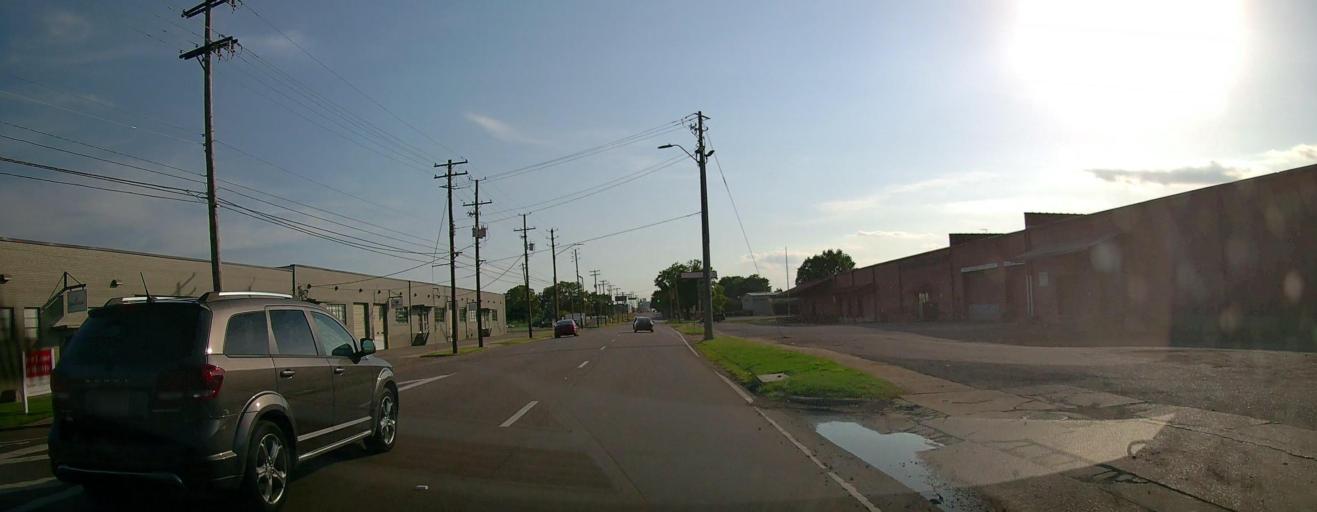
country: US
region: Alabama
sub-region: Jefferson County
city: Birmingham
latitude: 33.5206
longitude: -86.7806
